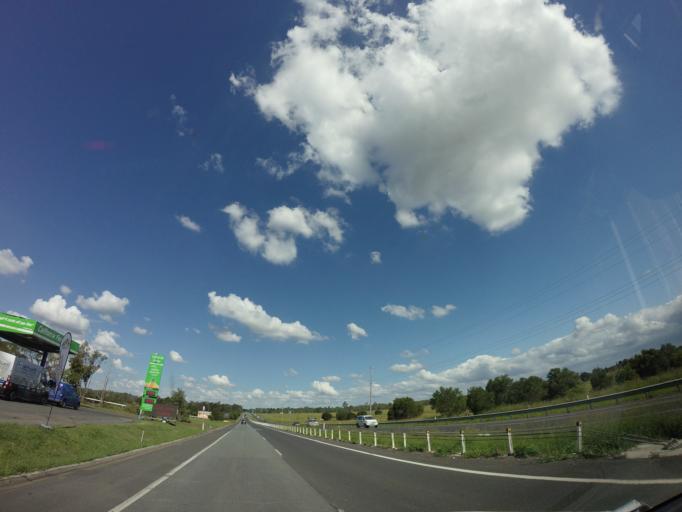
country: AU
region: Queensland
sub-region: Ipswich
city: Thagoona
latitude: -27.5727
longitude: 152.6474
